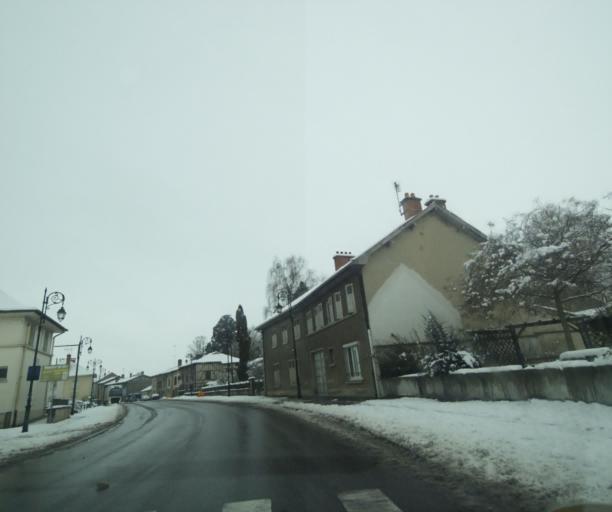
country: FR
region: Champagne-Ardenne
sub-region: Departement de la Haute-Marne
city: Montier-en-Der
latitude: 48.4787
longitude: 4.7686
